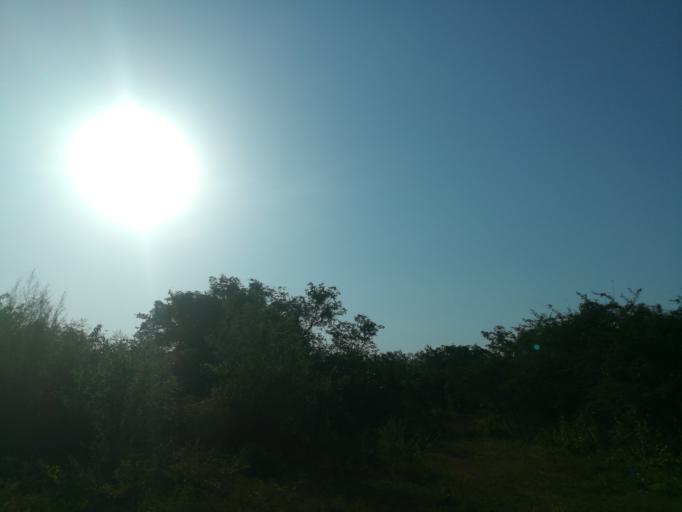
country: NG
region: Ogun
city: Abeokuta
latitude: 7.2490
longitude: 3.3005
